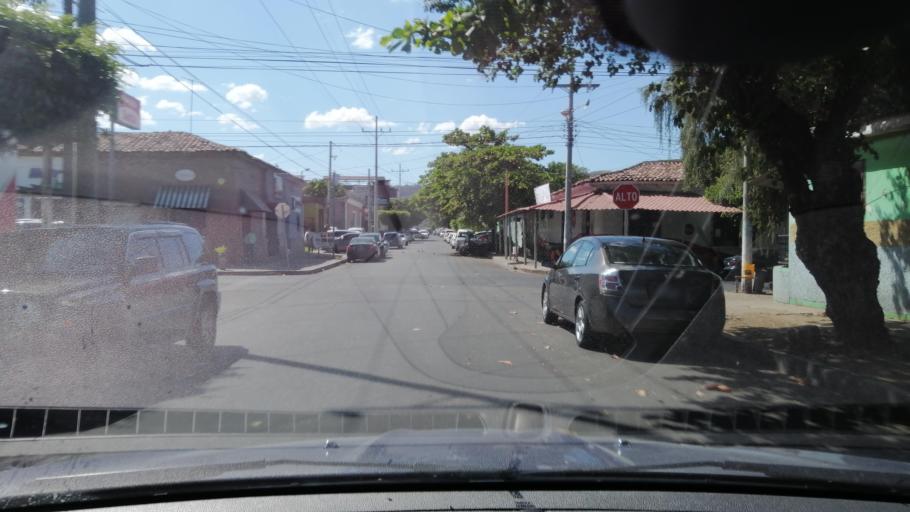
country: SV
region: Santa Ana
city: Santa Ana
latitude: 13.9837
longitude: -89.5574
